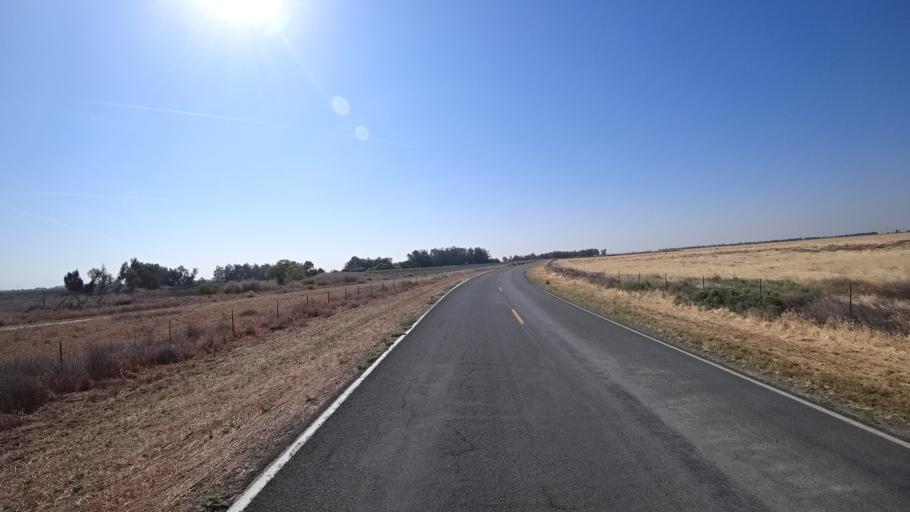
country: US
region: California
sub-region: Fresno County
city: Riverdale
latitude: 36.3699
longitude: -119.9209
